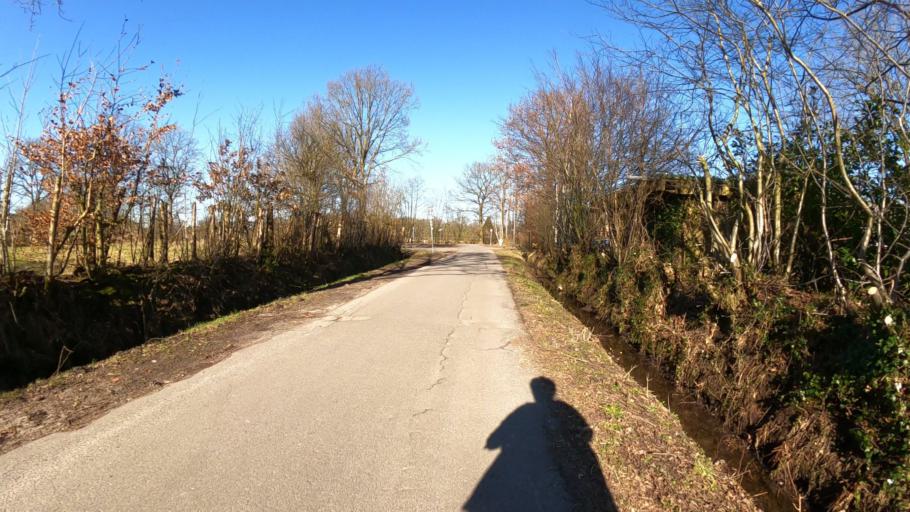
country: DE
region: Schleswig-Holstein
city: Kummerfeld
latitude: 53.6795
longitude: 9.7831
